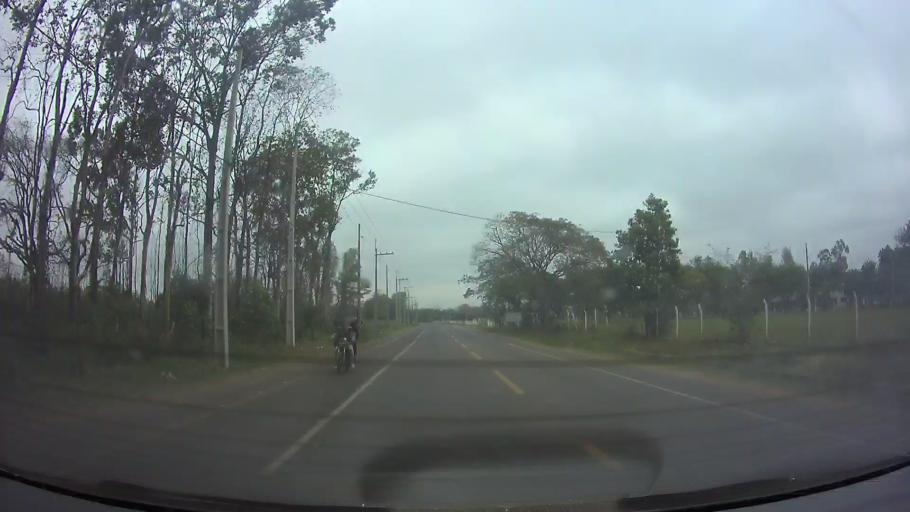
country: PY
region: Central
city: Limpio
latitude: -25.2213
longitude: -57.4178
